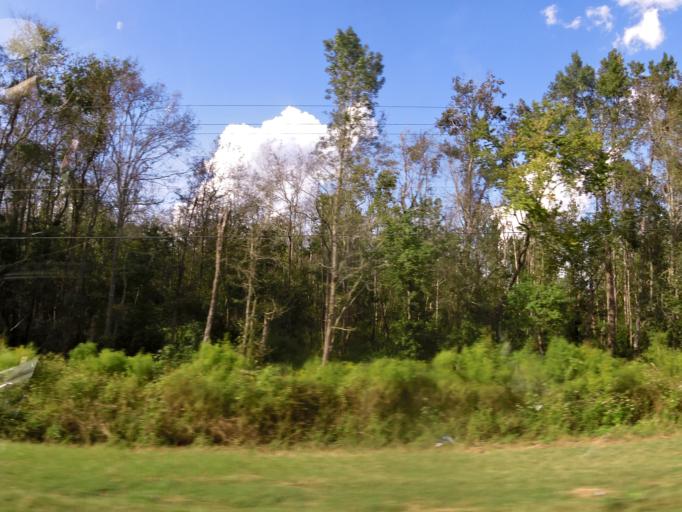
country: US
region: Georgia
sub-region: Brooks County
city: Quitman
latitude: 30.7854
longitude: -83.6102
